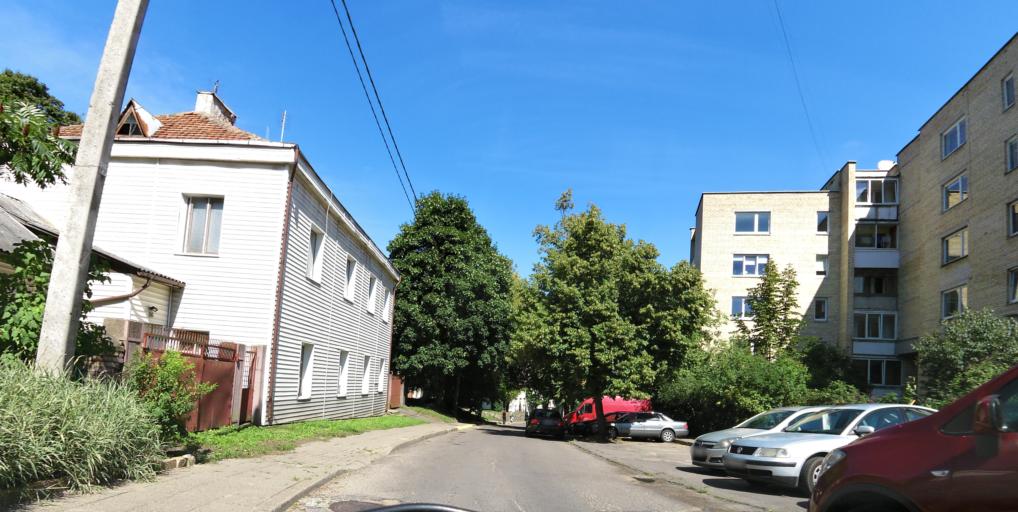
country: LT
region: Vilnius County
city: Naujamiestis
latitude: 54.6668
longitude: 25.2891
